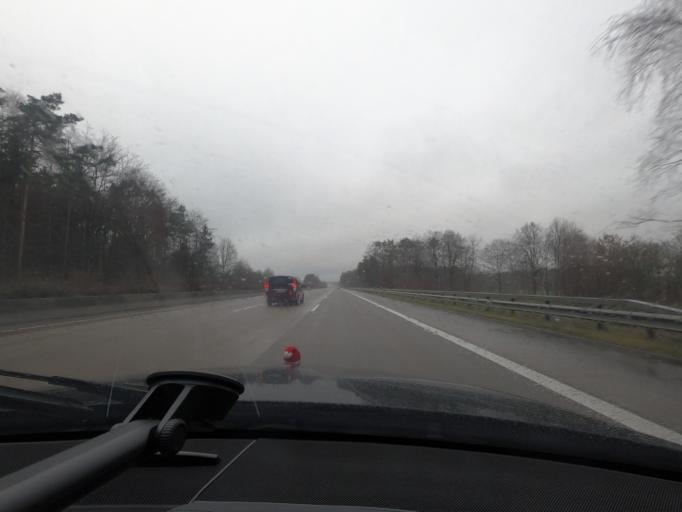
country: DE
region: Lower Saxony
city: Toppenstedt
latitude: 53.2826
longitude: 10.0801
